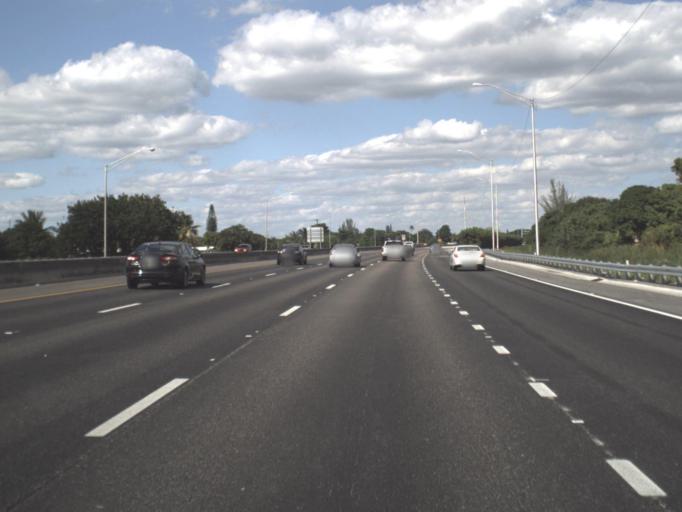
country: US
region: Florida
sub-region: Broward County
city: Miramar
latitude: 25.9839
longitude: -80.2298
